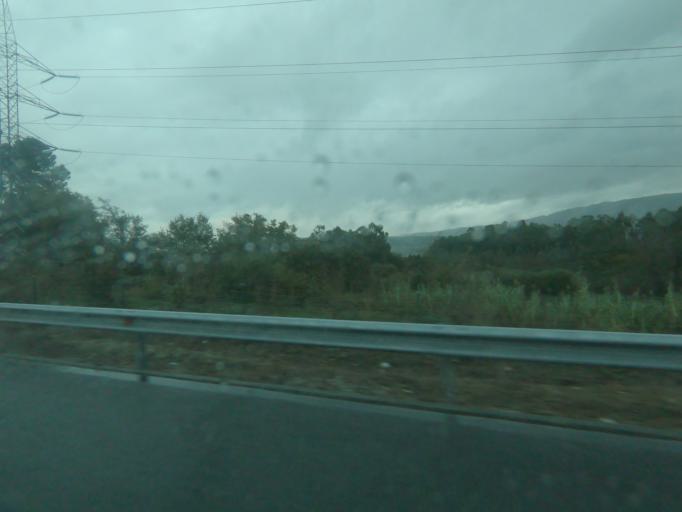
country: ES
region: Galicia
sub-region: Provincia de Pontevedra
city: Pontevedra
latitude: 42.3989
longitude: -8.6484
